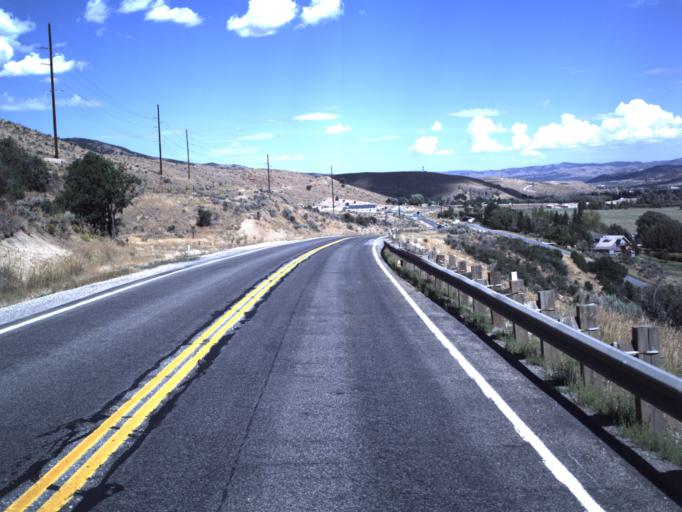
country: US
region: Utah
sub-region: Summit County
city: Coalville
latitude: 40.7933
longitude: -111.4098
